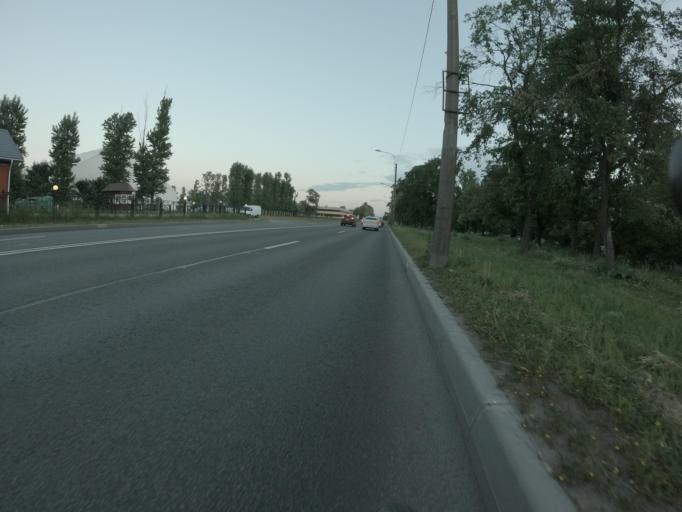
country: RU
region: St.-Petersburg
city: Dachnoye
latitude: 59.8420
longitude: 30.2750
